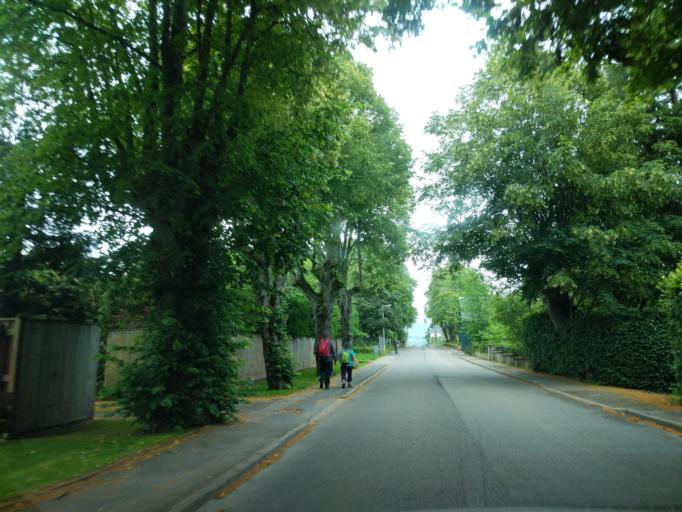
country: GB
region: Scotland
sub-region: Highland
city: Grantown on Spey
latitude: 57.3322
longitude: -3.6121
